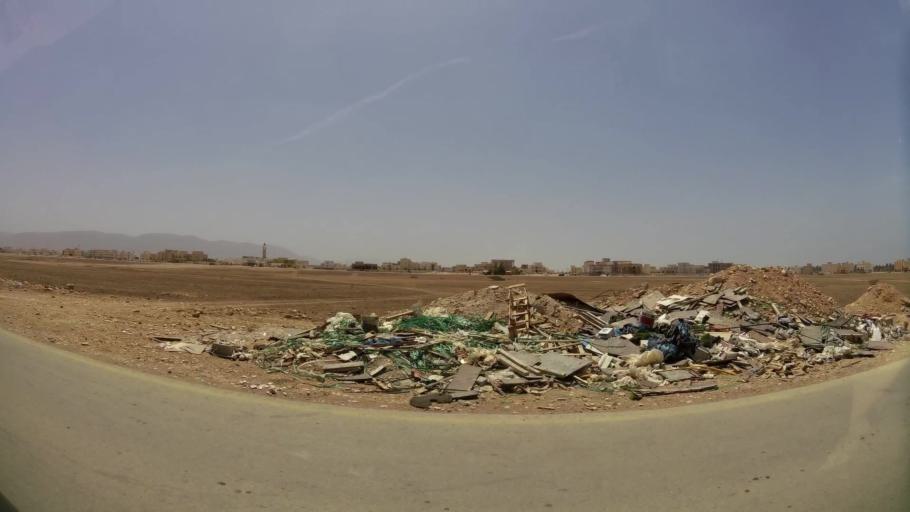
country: OM
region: Zufar
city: Salalah
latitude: 17.0543
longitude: 54.2075
